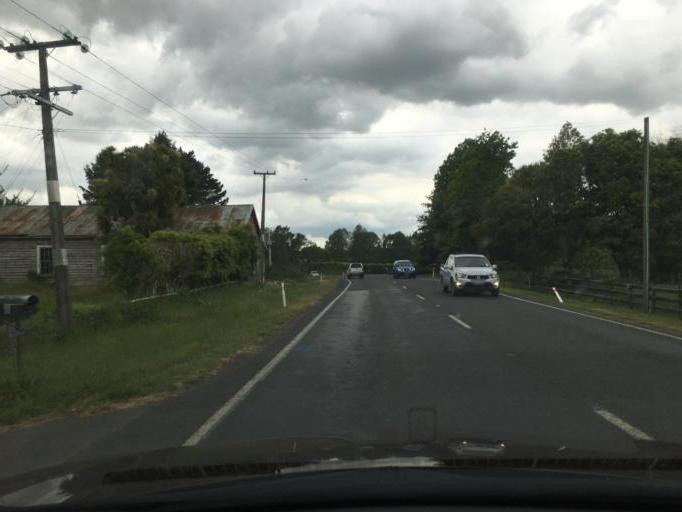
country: NZ
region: Waikato
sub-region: Waipa District
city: Cambridge
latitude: -37.9158
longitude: 175.4470
